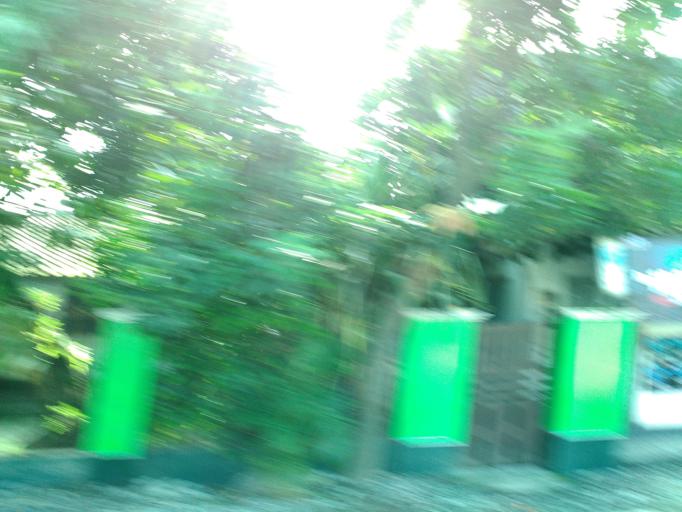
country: ID
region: Central Java
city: Gatak
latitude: -7.6050
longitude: 110.7027
